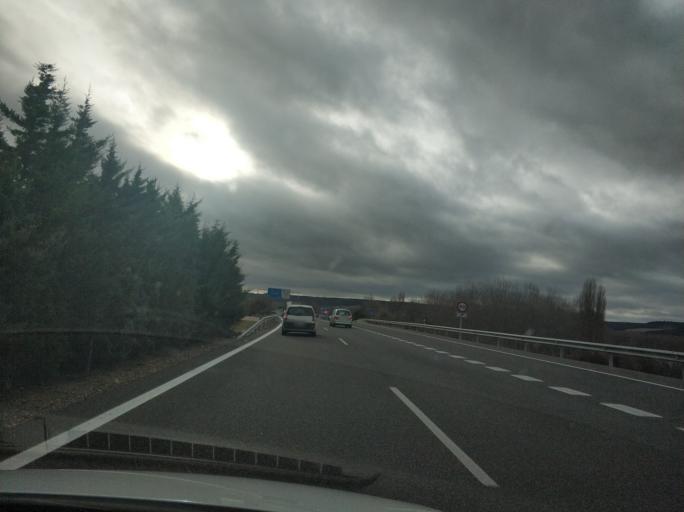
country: ES
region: Castille and Leon
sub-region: Provincia de Palencia
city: Venta de Banos
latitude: 41.9372
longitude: -4.4942
